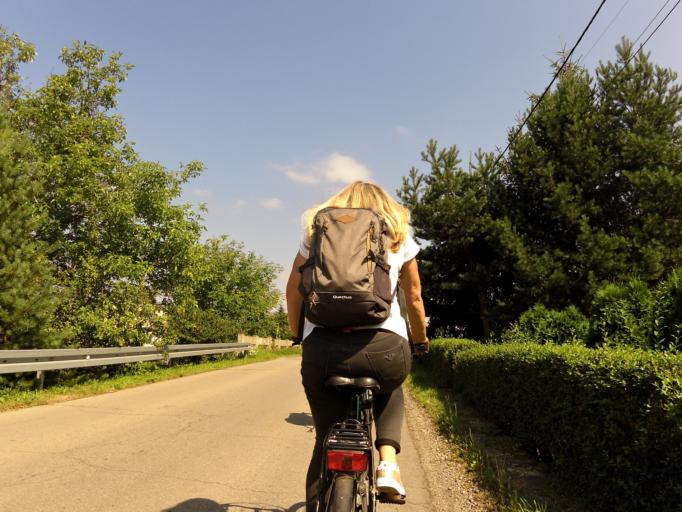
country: PL
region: Silesian Voivodeship
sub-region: Powiat zywiecki
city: Ciecina
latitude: 49.6209
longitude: 19.1442
